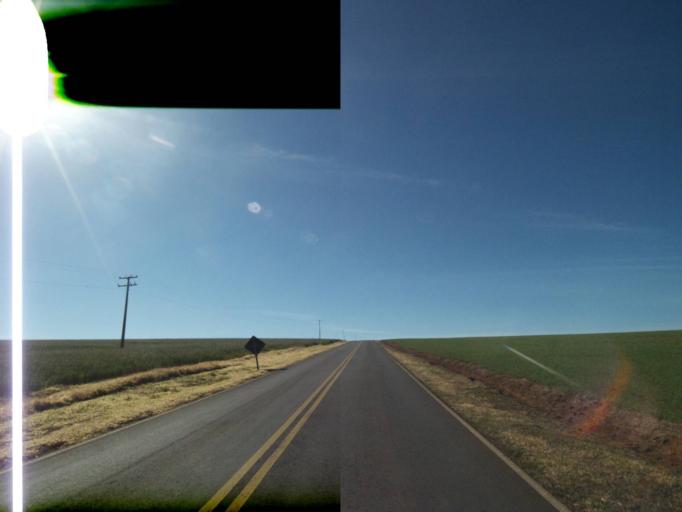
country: BR
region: Parana
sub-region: Tibagi
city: Tibagi
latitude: -24.5201
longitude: -50.3391
